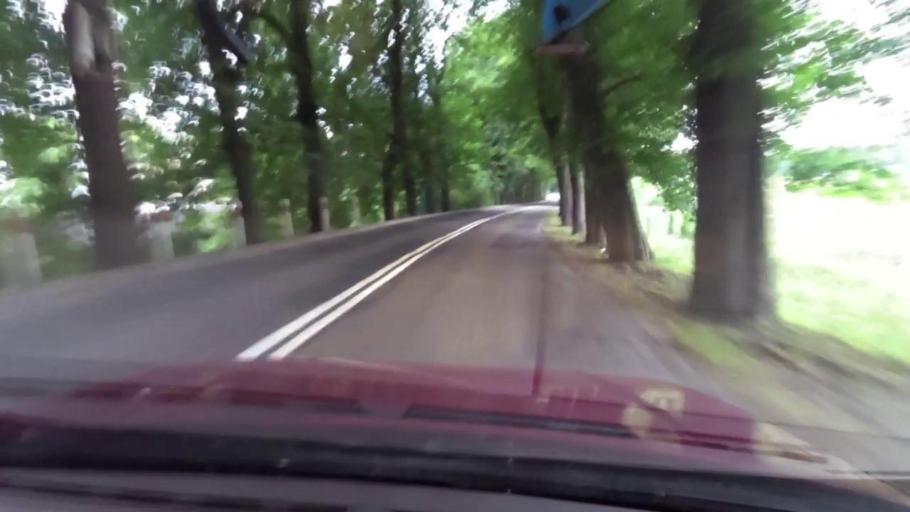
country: PL
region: West Pomeranian Voivodeship
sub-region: Powiat koszalinski
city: Sianow
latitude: 54.1863
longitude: 16.2432
